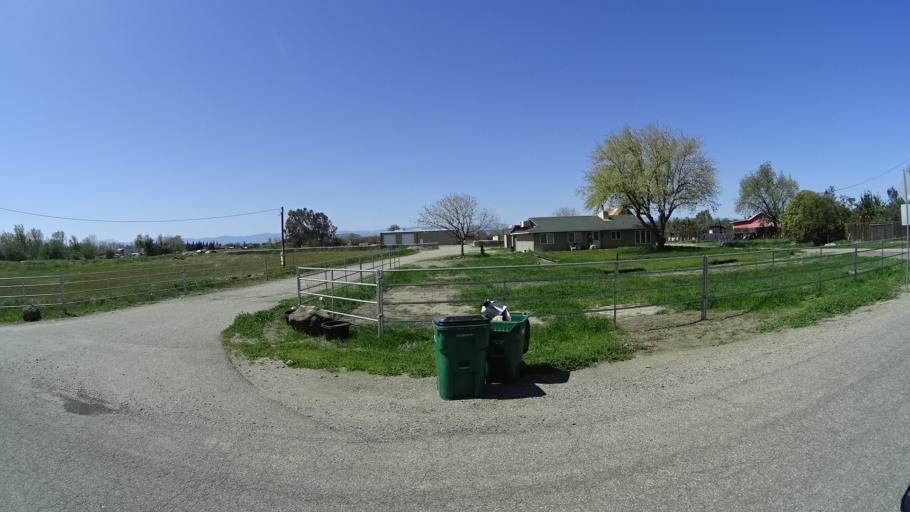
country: US
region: California
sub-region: Glenn County
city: Orland
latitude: 39.7674
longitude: -122.2295
